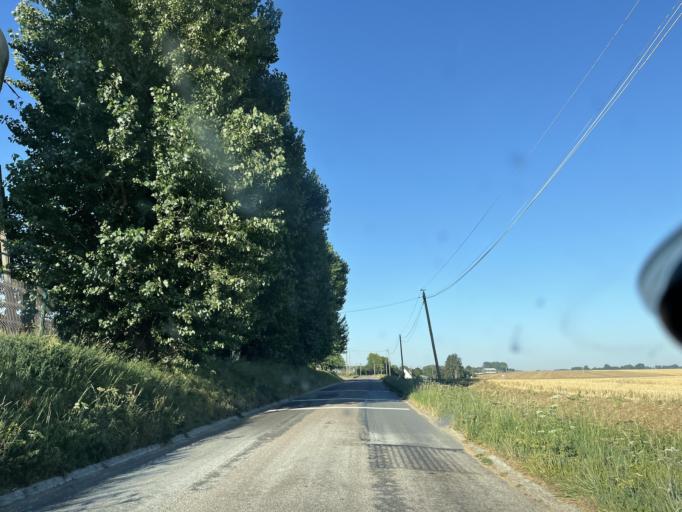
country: FR
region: Haute-Normandie
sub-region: Departement de la Seine-Maritime
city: Fauville-en-Caux
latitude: 49.6097
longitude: 0.5992
